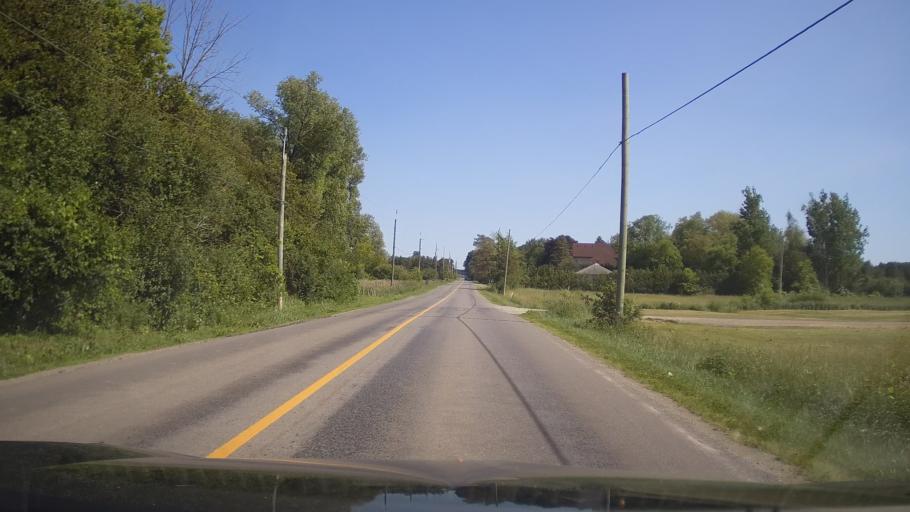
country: CA
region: Ontario
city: Oshawa
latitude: 43.9566
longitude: -78.7292
